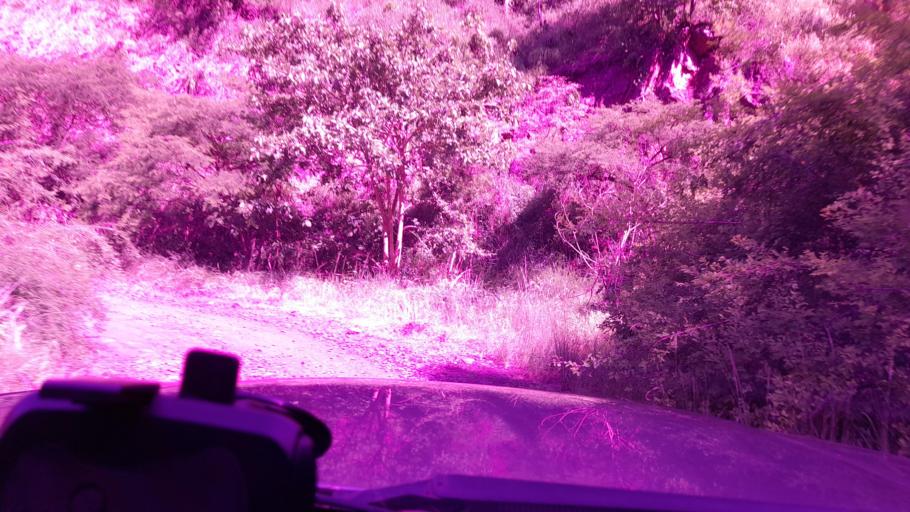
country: ET
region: Southern Nations, Nationalities, and People's Region
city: K'olito
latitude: 7.7725
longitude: 37.5536
